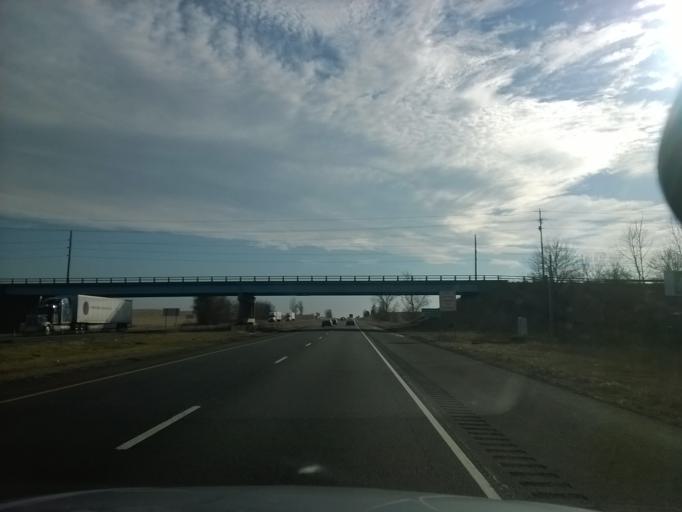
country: US
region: Indiana
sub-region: Johnson County
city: Edinburgh
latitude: 39.3484
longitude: -85.9424
